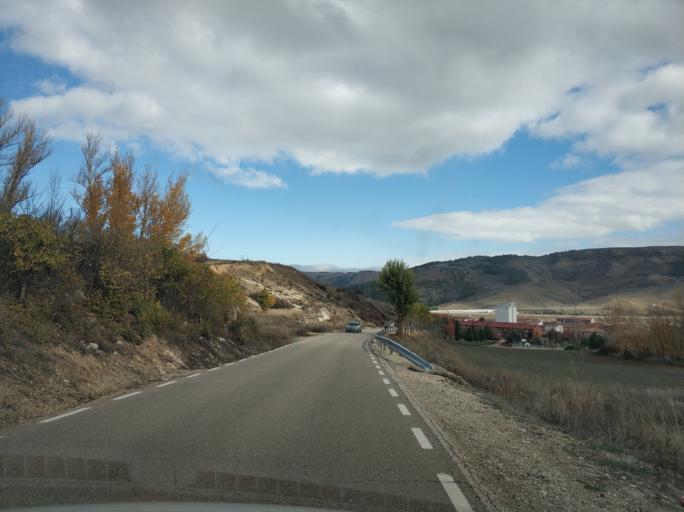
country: ES
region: Castille and Leon
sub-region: Provincia de Soria
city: Medinaceli
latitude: 41.1660
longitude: -2.4297
